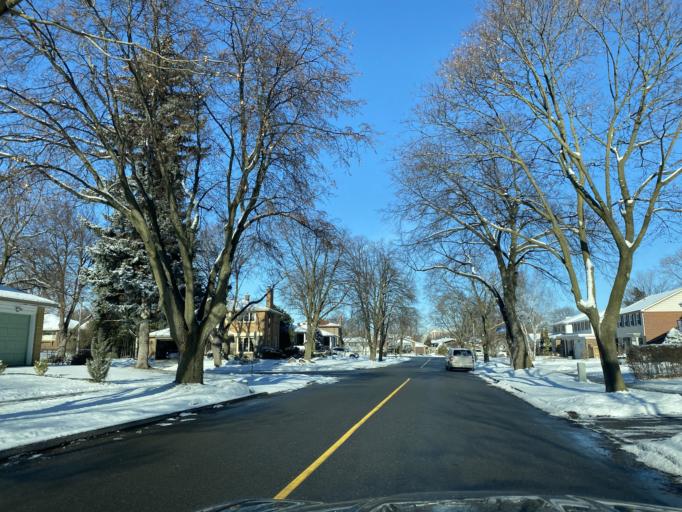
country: CA
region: Ontario
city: Scarborough
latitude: 43.7838
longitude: -79.3126
